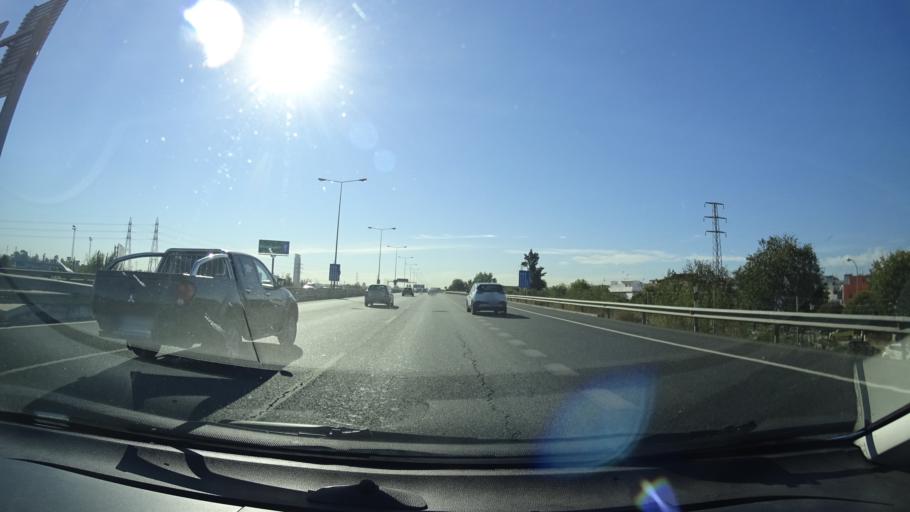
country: ES
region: Andalusia
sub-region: Provincia de Sevilla
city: Camas
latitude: 37.4072
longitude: -6.0321
